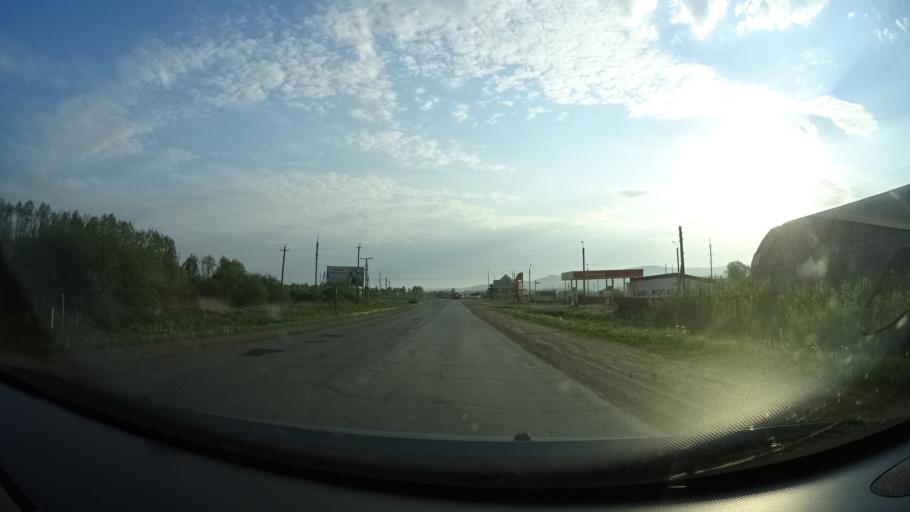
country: RU
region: Perm
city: Barda
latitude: 56.9434
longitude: 55.5904
